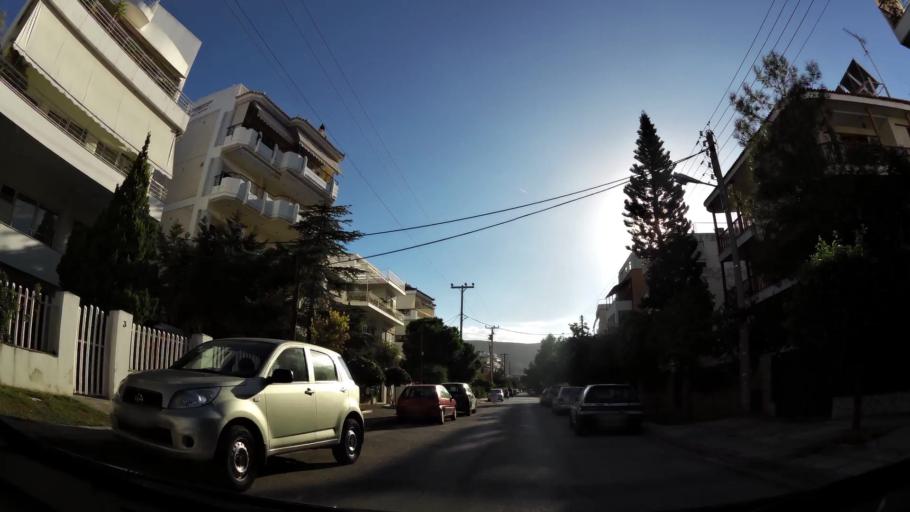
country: GR
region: Attica
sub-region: Nomarchia Athinas
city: Glyfada
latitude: 37.8740
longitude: 23.7513
